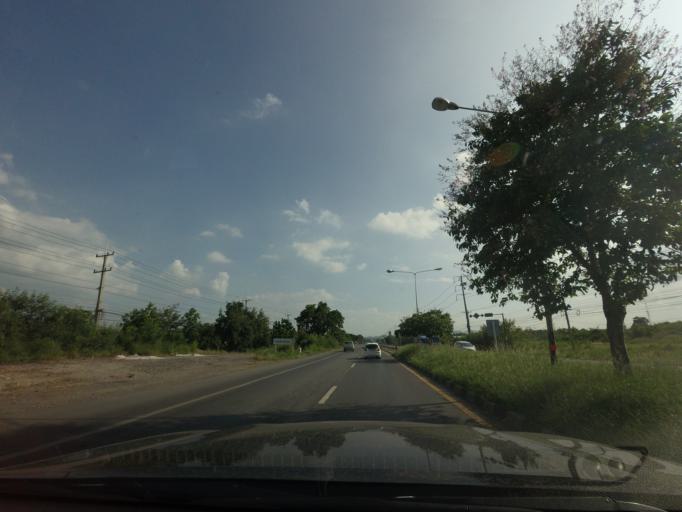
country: TH
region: Lop Buri
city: Phatthana Nikhom
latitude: 14.8546
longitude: 100.9096
